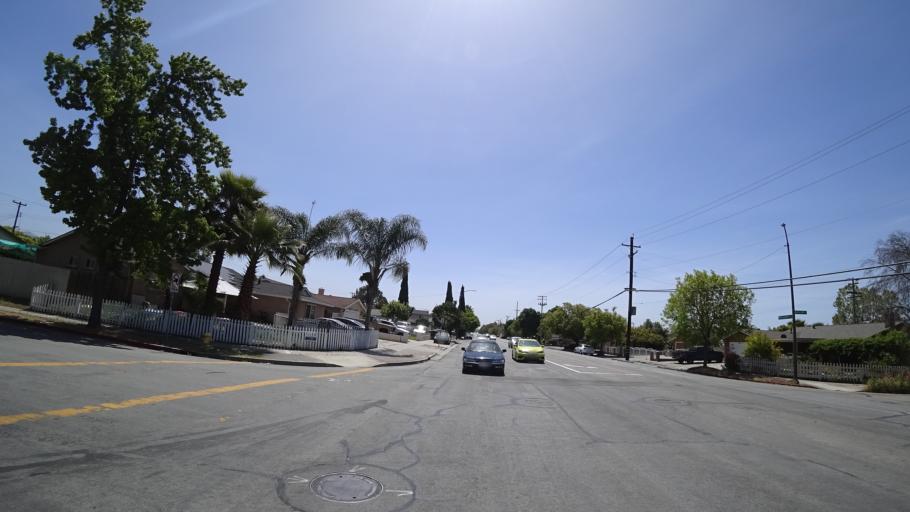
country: US
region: California
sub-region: Santa Clara County
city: Seven Trees
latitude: 37.3238
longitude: -121.8449
